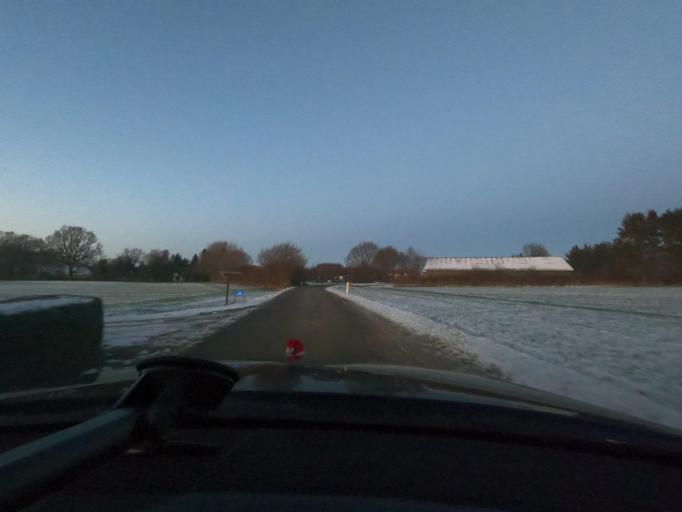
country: DK
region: South Denmark
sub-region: Sonderborg Kommune
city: Horuphav
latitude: 54.8672
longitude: 9.9504
